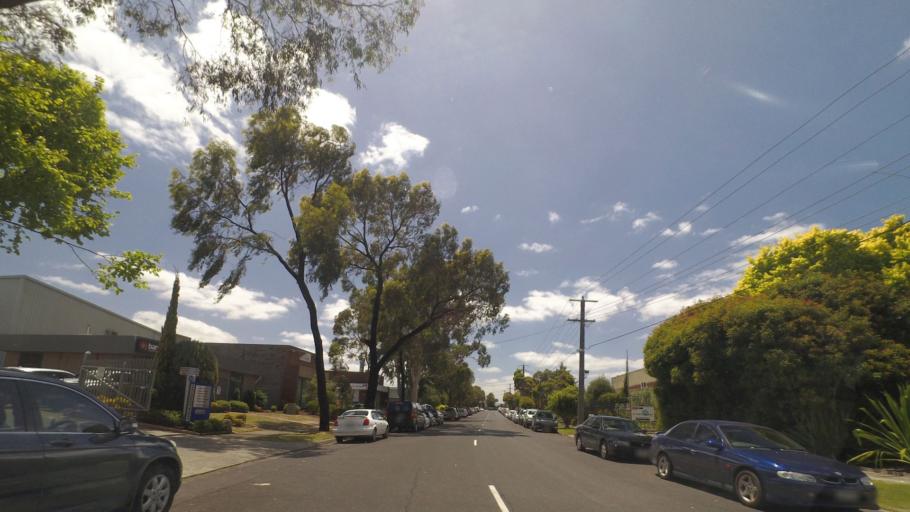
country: AU
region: Victoria
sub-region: Maroondah
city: Bayswater North
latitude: -37.8176
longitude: 145.2978
